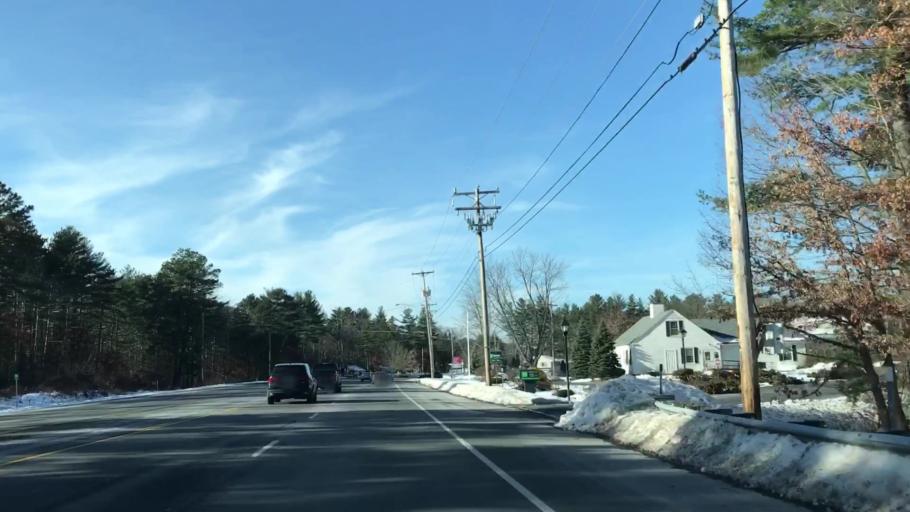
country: US
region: New Hampshire
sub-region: Hillsborough County
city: Milford
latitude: 42.8150
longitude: -71.5978
